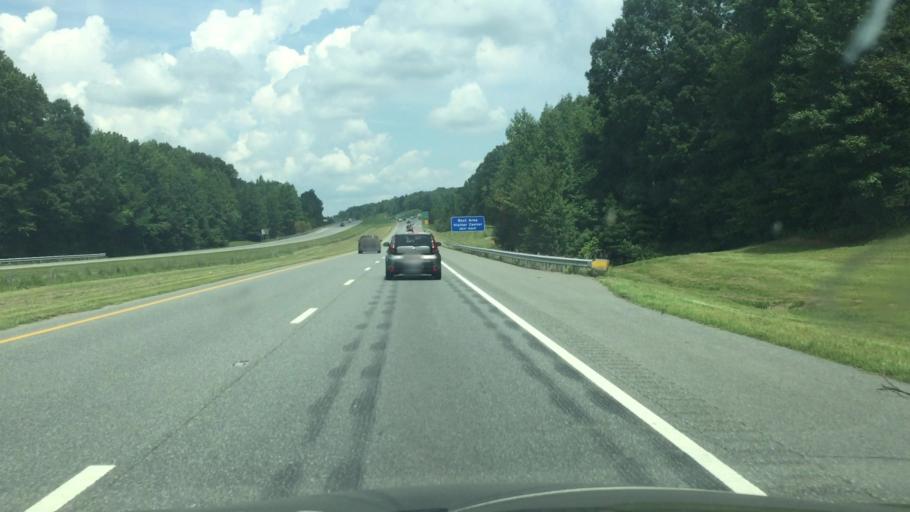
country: US
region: North Carolina
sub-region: Montgomery County
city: Biscoe
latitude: 35.5072
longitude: -79.7811
